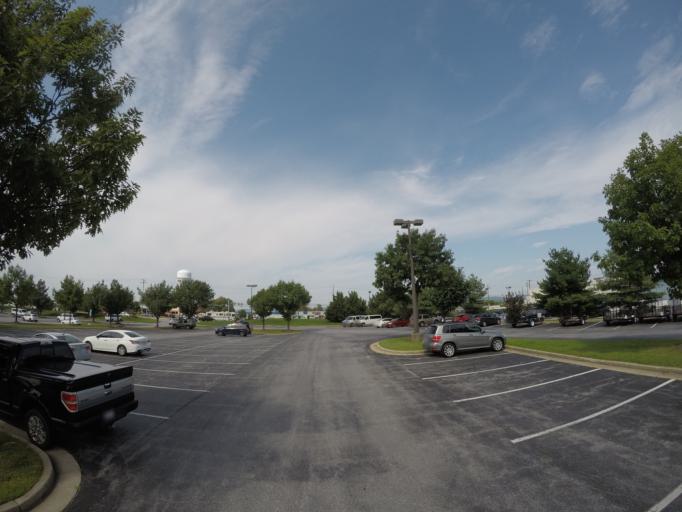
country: US
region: Maryland
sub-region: Frederick County
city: Frederick
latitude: 39.3886
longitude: -77.4082
